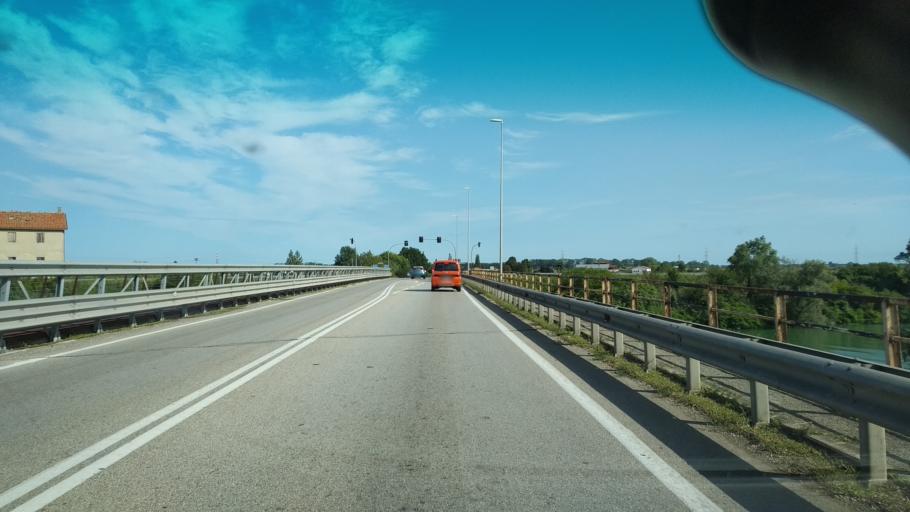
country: IT
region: Veneto
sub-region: Provincia di Padova
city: Codevigo
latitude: 45.2678
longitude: 12.1064
